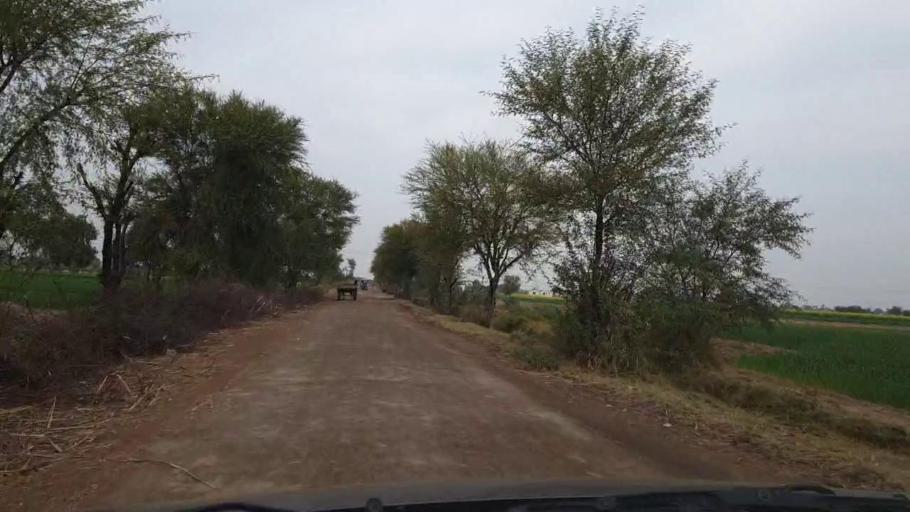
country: PK
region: Sindh
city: Sanghar
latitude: 26.0995
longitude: 68.8966
